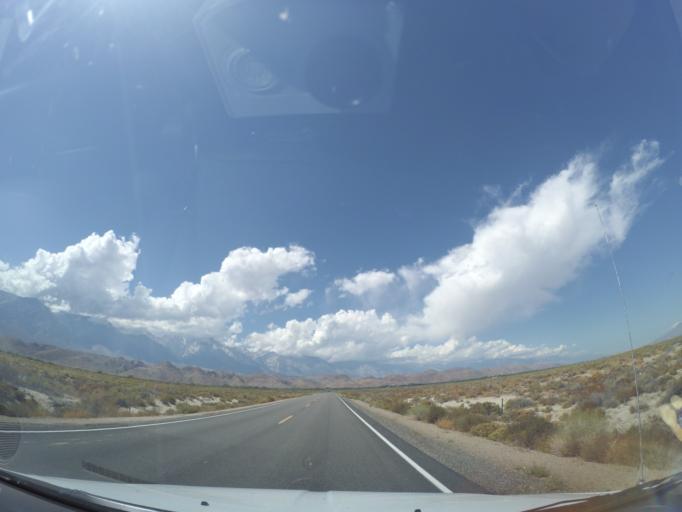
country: US
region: California
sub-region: Inyo County
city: Lone Pine
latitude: 36.5771
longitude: -118.0284
